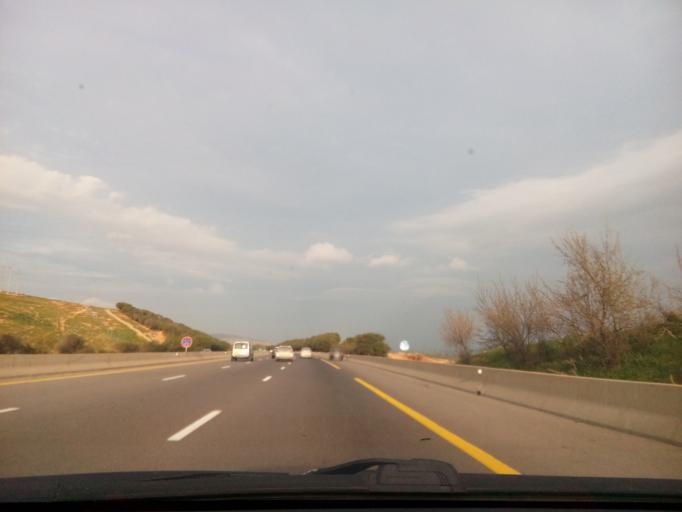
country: DZ
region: Relizane
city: Relizane
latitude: 35.7578
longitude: 0.3630
